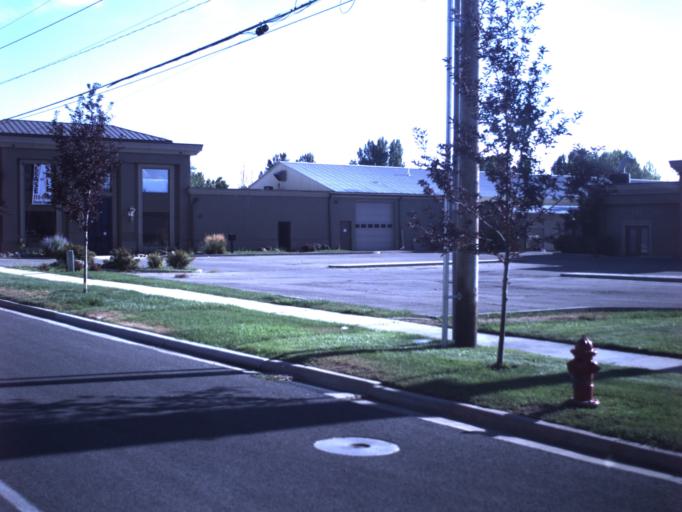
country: US
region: Utah
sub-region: Utah County
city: Springville
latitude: 40.1781
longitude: -111.6107
